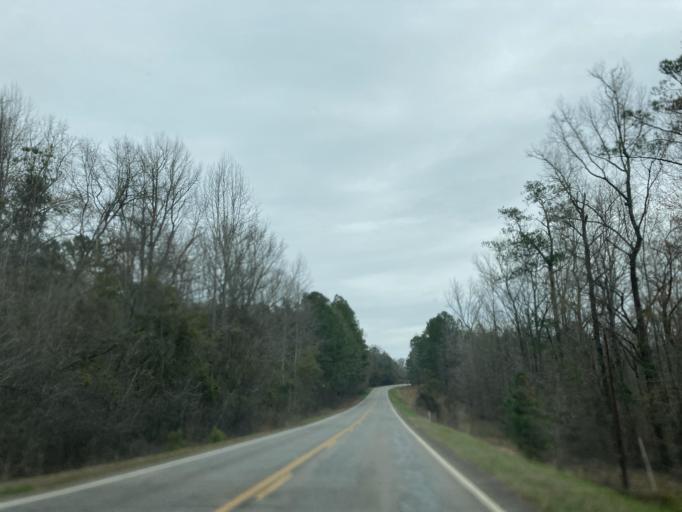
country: US
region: Georgia
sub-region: Jones County
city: Gray
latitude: 32.9723
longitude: -83.6304
